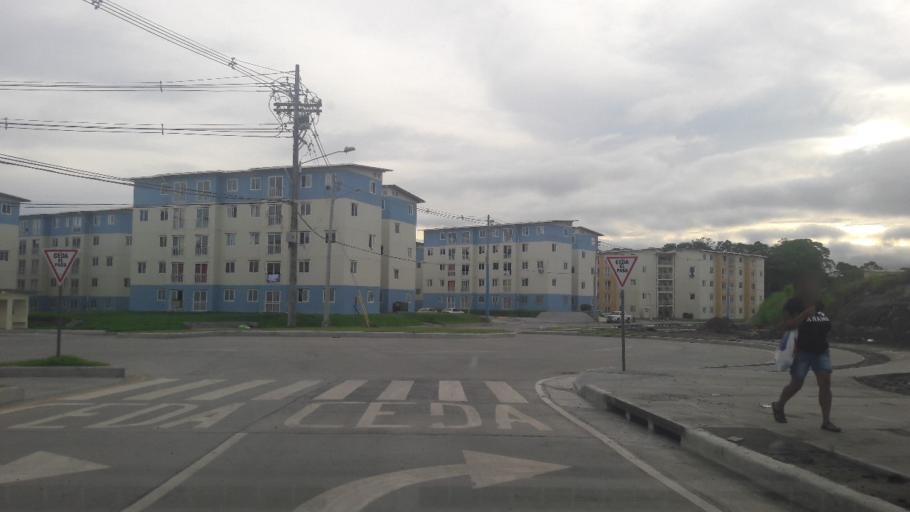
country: PA
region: Colon
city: Cativa
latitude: 9.3705
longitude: -79.8507
